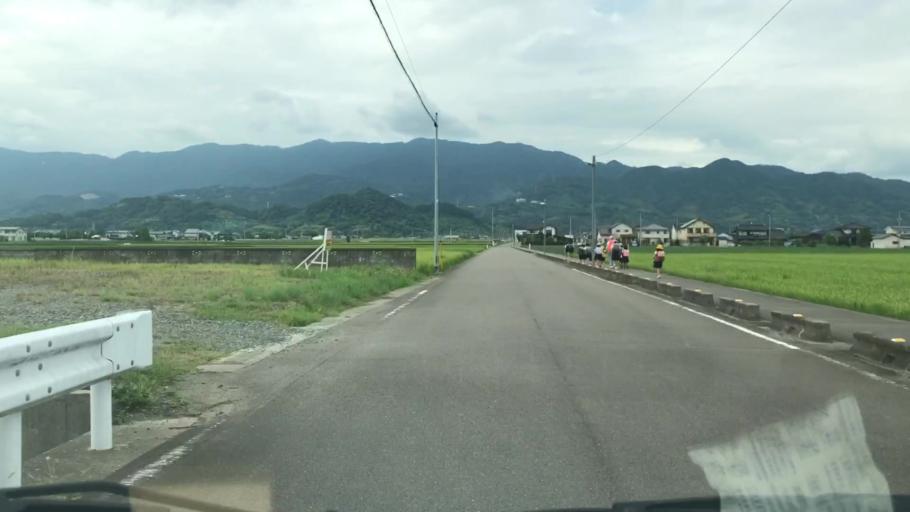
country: JP
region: Saga Prefecture
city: Saga-shi
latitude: 33.2831
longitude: 130.2260
